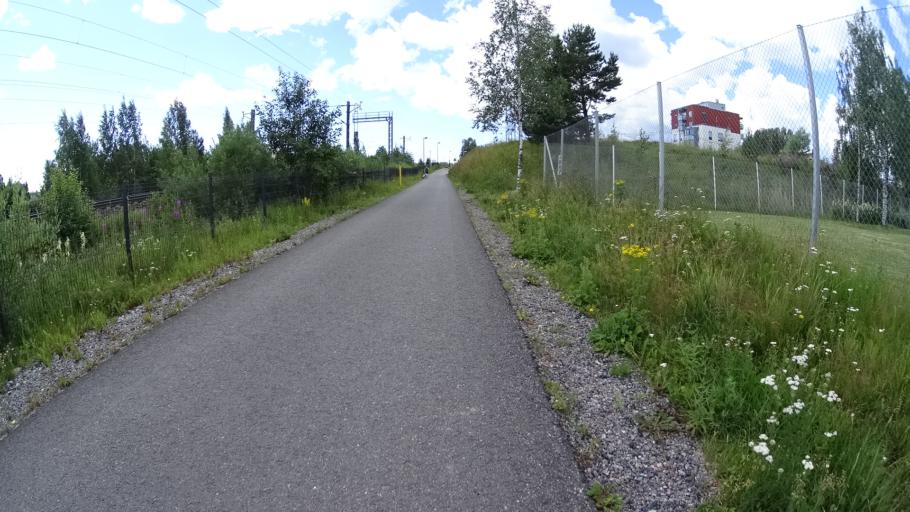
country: FI
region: Uusimaa
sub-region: Helsinki
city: Kirkkonummi
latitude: 60.1562
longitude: 24.5371
